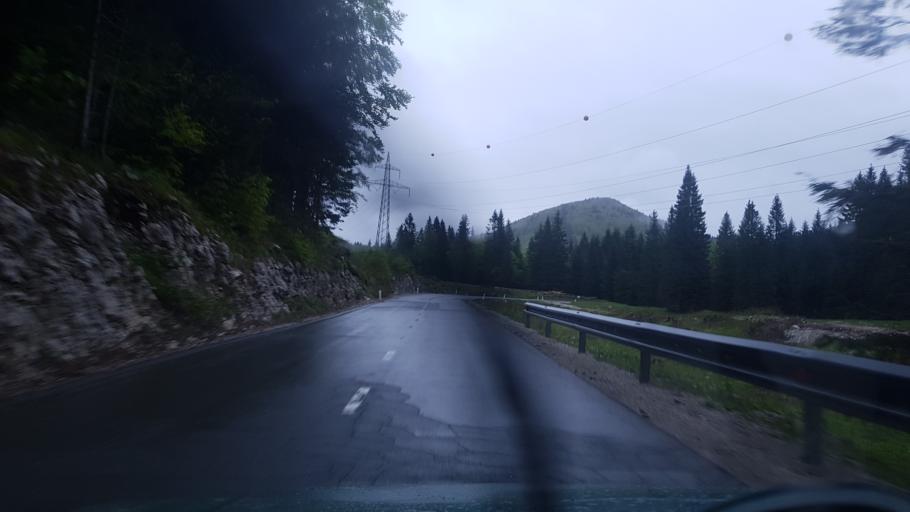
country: SI
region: Bohinj
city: Bohinjska Bistrica
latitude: 46.2455
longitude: 14.0063
